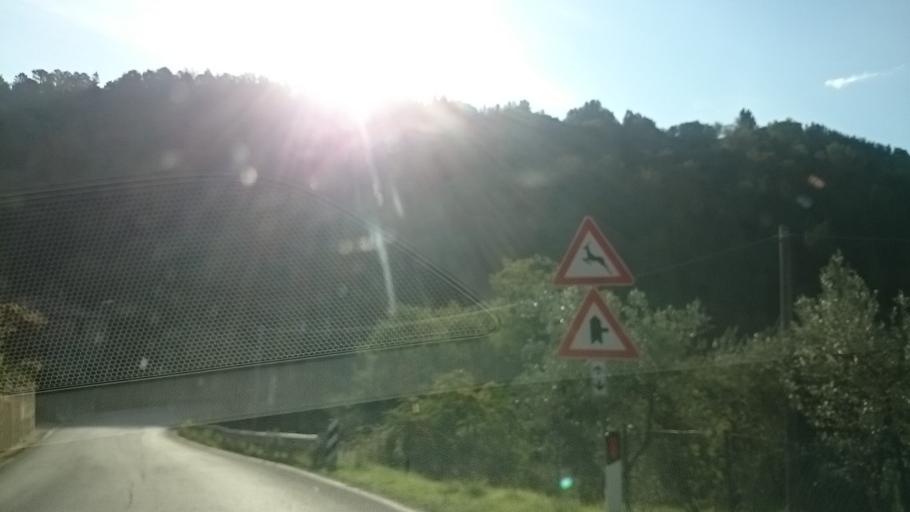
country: IT
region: Tuscany
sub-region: Province of Florence
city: Reggello
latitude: 43.7055
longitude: 11.5234
